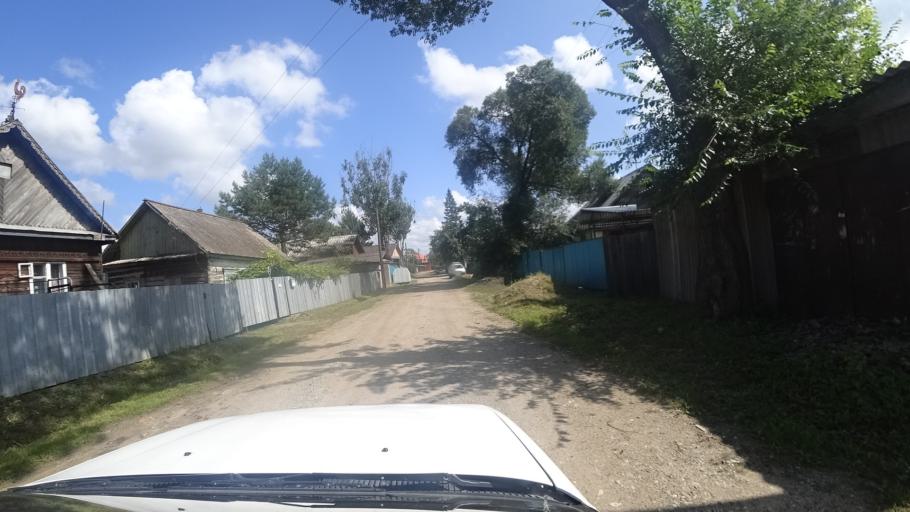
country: RU
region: Primorskiy
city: Dal'nerechensk
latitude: 45.9252
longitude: 133.7163
